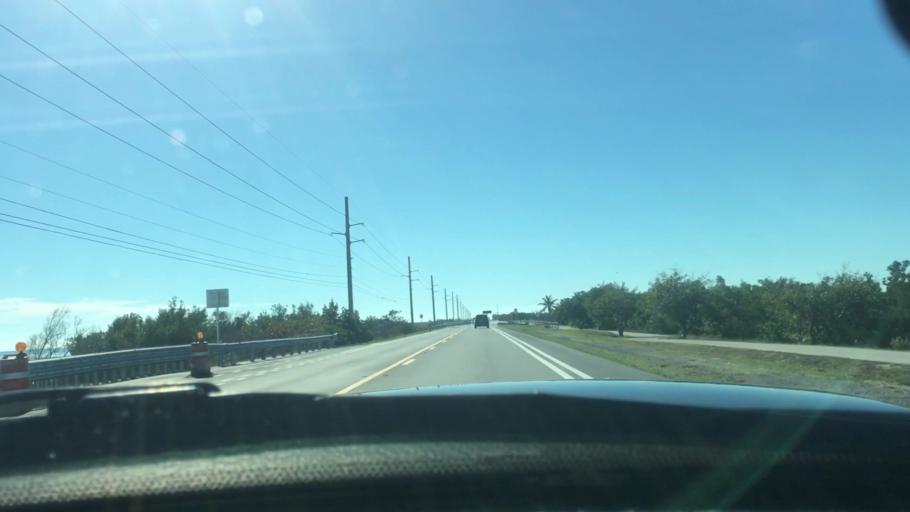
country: US
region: Florida
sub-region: Monroe County
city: Big Pine Key
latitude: 24.6807
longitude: -81.2321
